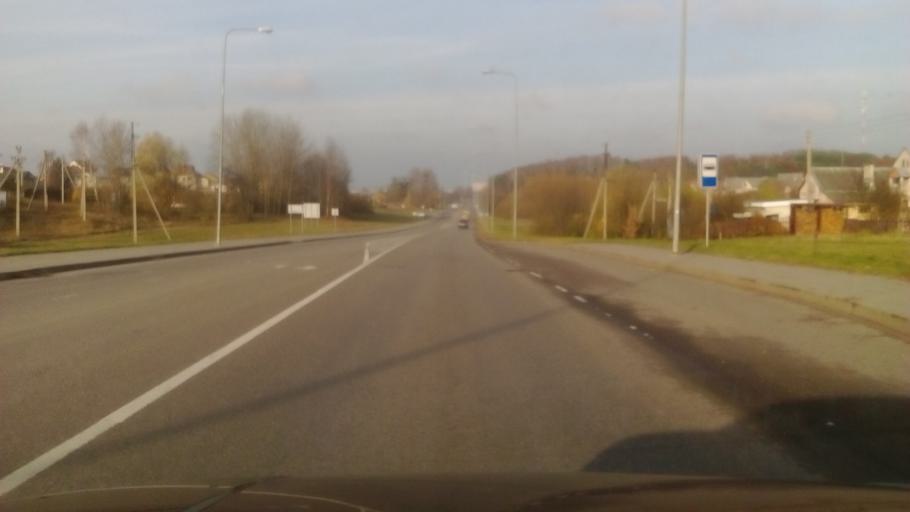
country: LT
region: Alytaus apskritis
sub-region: Alytus
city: Alytus
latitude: 54.3972
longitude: 23.9997
